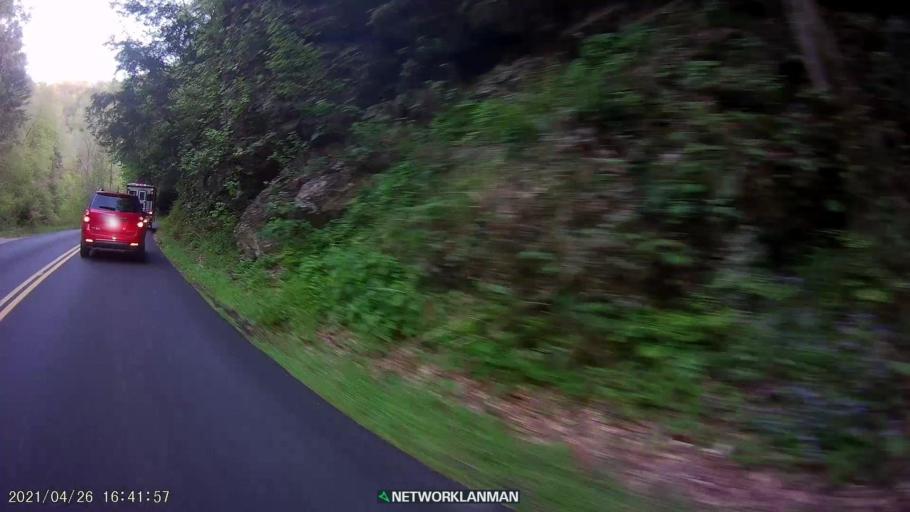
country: US
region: Tennessee
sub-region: Sevier County
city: Pigeon Forge
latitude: 35.6663
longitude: -83.6895
